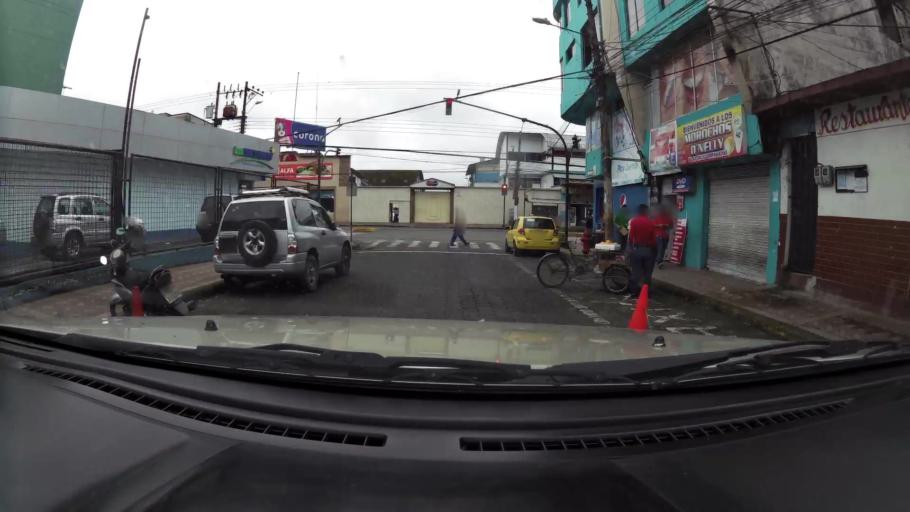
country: EC
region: Santo Domingo de los Tsachilas
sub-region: Canton Santo Domingo de los Colorados
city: Santo Domingo de los Colorados
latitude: -0.2519
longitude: -79.1651
